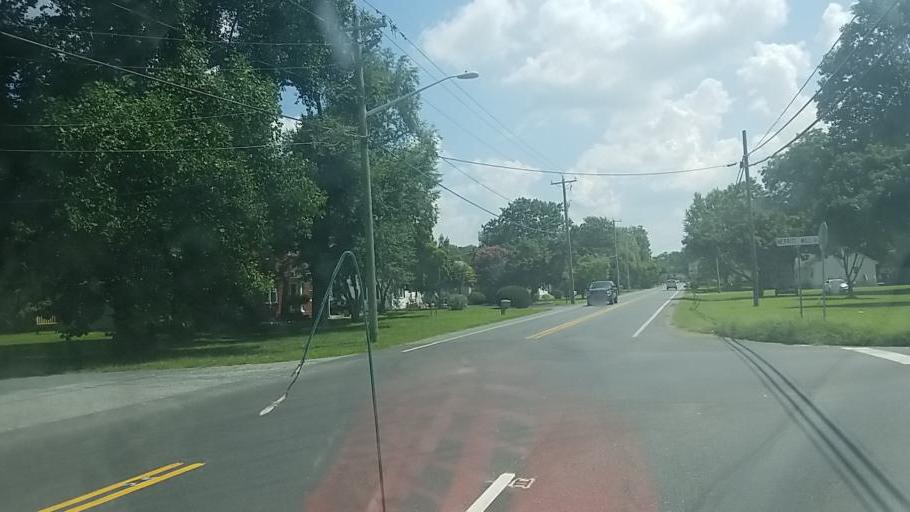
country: US
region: Maryland
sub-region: Wicomico County
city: Salisbury
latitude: 38.3732
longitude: -75.5531
